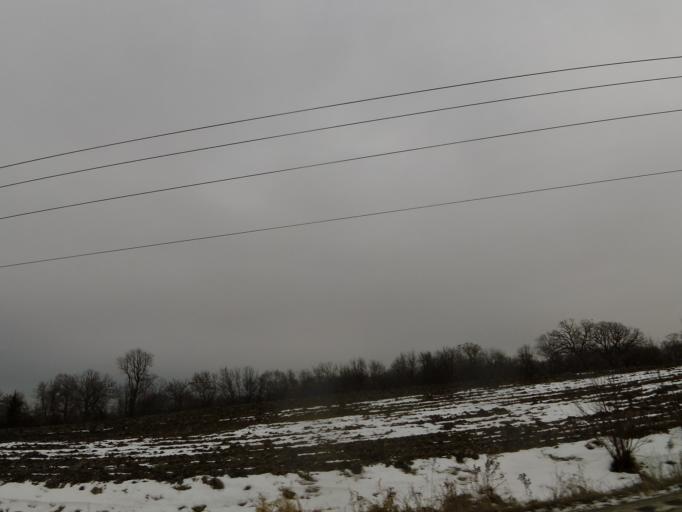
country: US
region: Minnesota
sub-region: Carver County
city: Waconia
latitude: 44.8136
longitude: -93.7882
